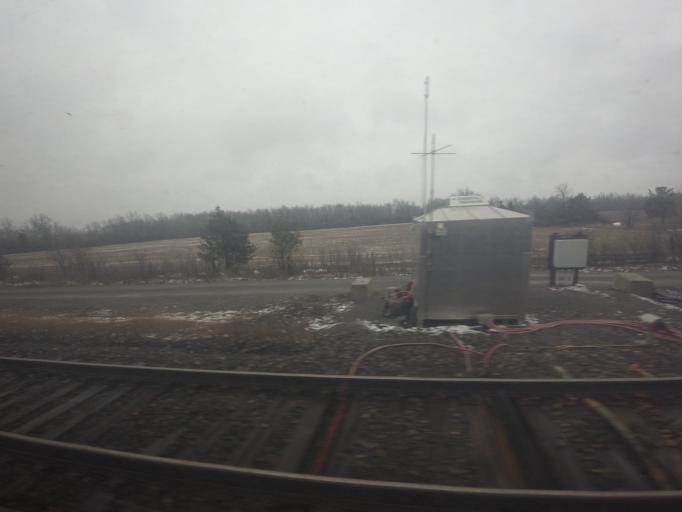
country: CA
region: Ontario
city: Deseronto
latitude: 44.2186
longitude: -77.1559
